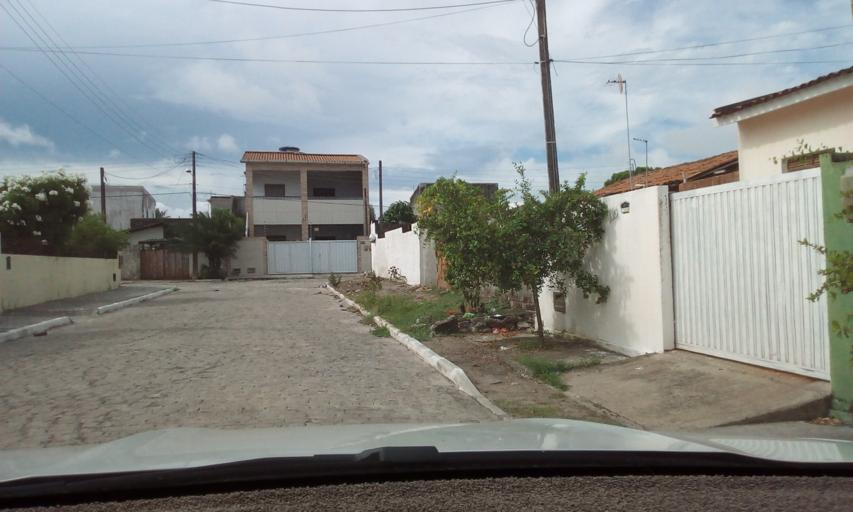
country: BR
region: Paraiba
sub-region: Joao Pessoa
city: Joao Pessoa
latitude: -7.1751
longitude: -34.8313
